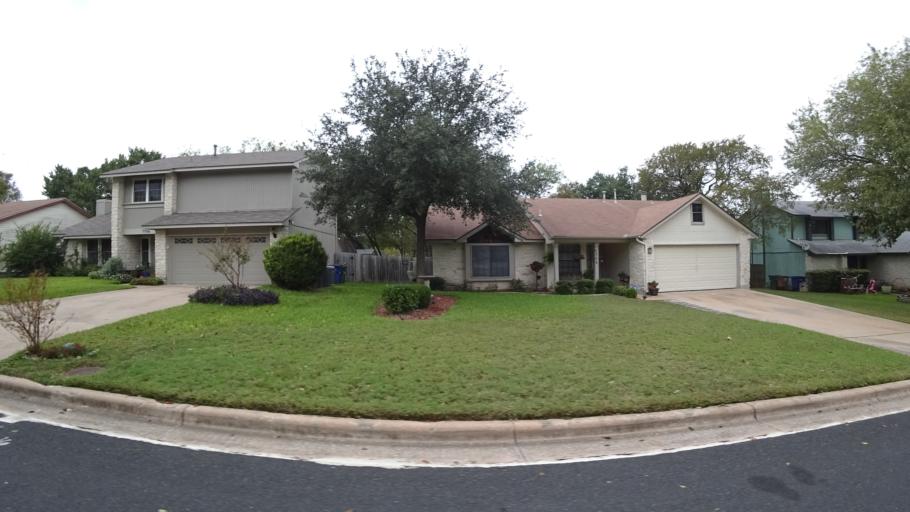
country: US
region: Texas
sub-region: Travis County
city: Shady Hollow
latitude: 30.2089
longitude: -97.8433
